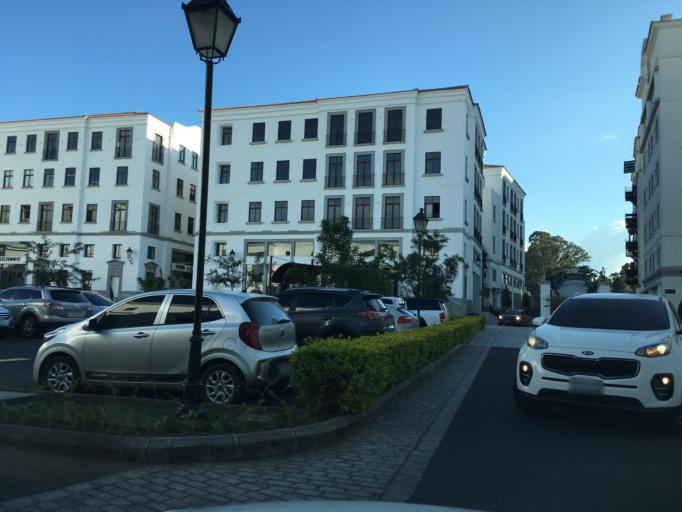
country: GT
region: Guatemala
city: Guatemala City
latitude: 14.6108
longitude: -90.4850
